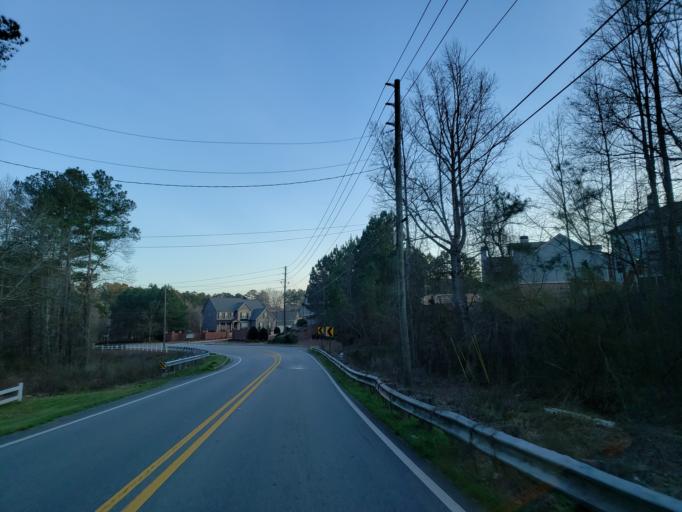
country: US
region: Georgia
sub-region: Cobb County
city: Acworth
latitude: 34.0011
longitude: -84.7372
